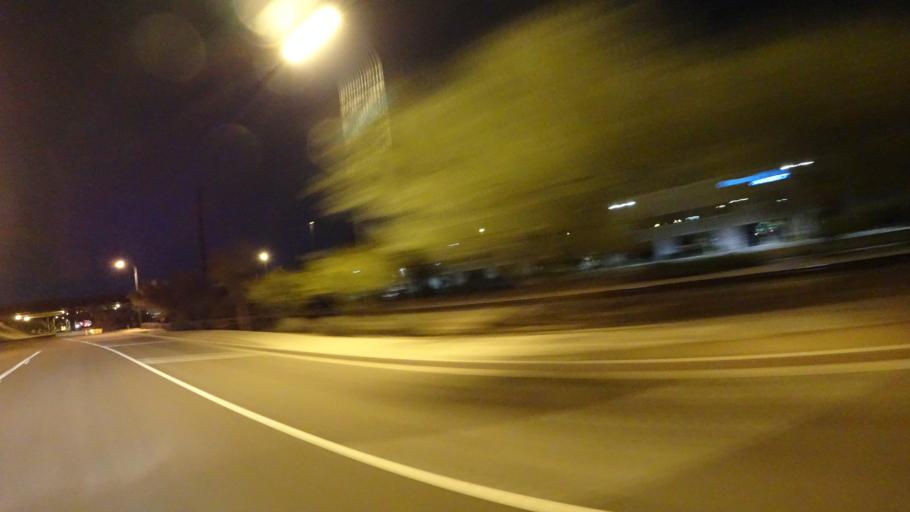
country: US
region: Arizona
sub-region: Maricopa County
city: Guadalupe
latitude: 33.2938
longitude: -111.9631
